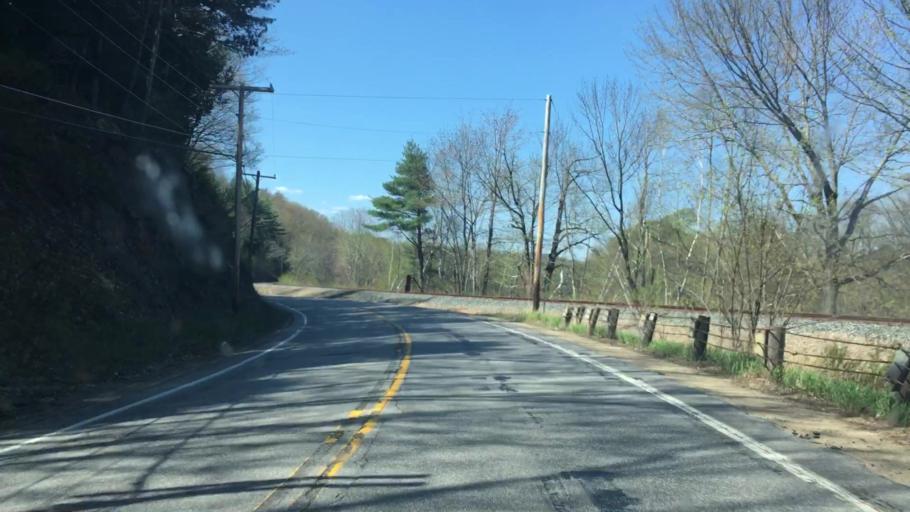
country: US
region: New Hampshire
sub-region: Grafton County
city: Plymouth
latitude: 43.7389
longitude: -71.6764
